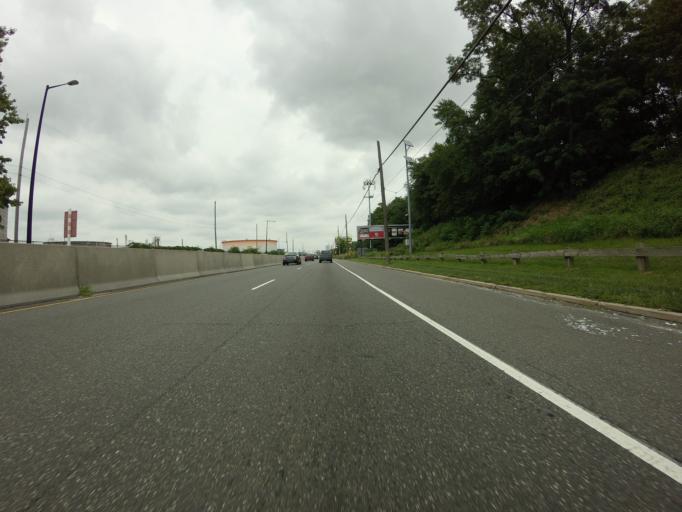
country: US
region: New Jersey
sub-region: Gloucester County
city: National Park
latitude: 39.9095
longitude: -75.1931
